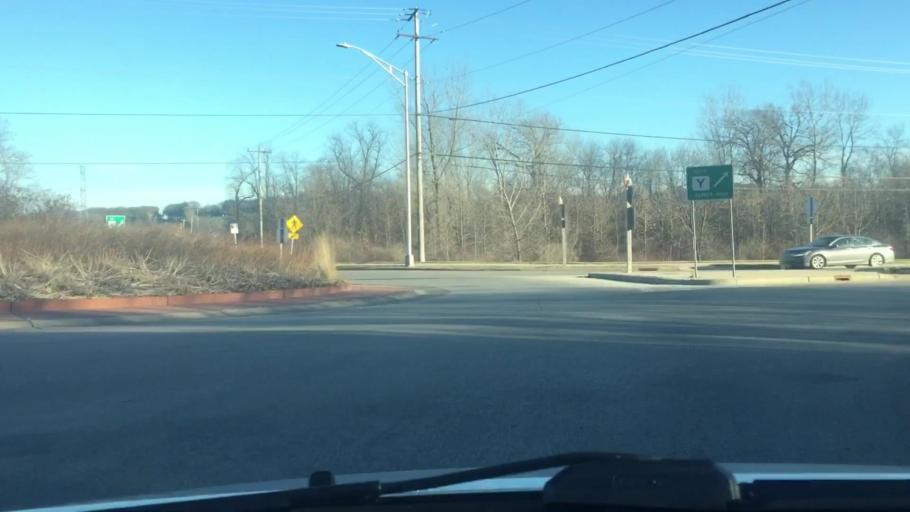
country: US
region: Wisconsin
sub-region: Waukesha County
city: Brookfield
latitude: 43.0613
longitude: -88.1665
